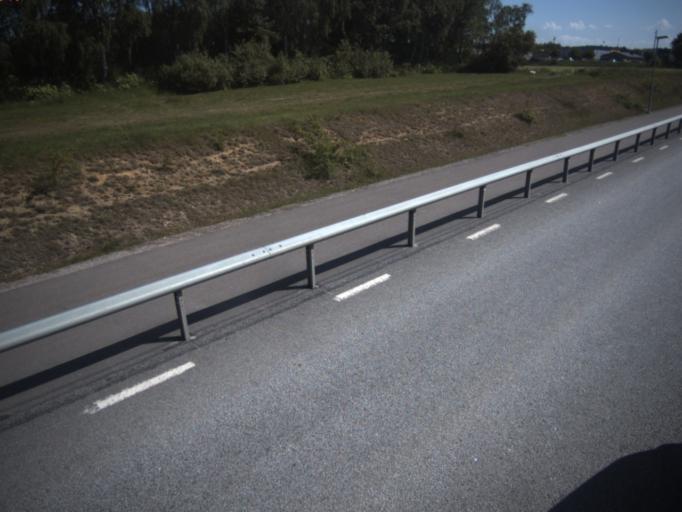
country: SE
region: Skane
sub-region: Helsingborg
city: Rydeback
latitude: 56.0025
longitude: 12.7682
